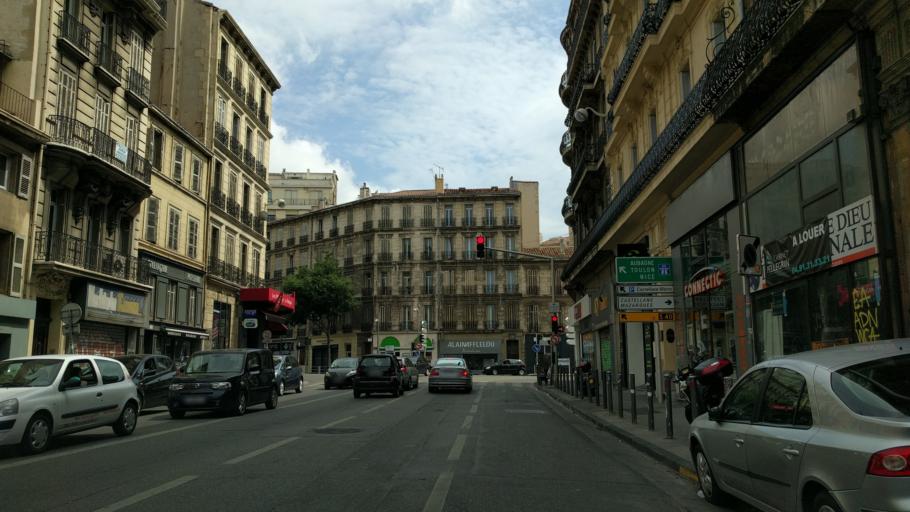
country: FR
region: Provence-Alpes-Cote d'Azur
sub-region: Departement des Bouches-du-Rhone
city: Marseille 06
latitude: 43.2869
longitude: 5.3852
